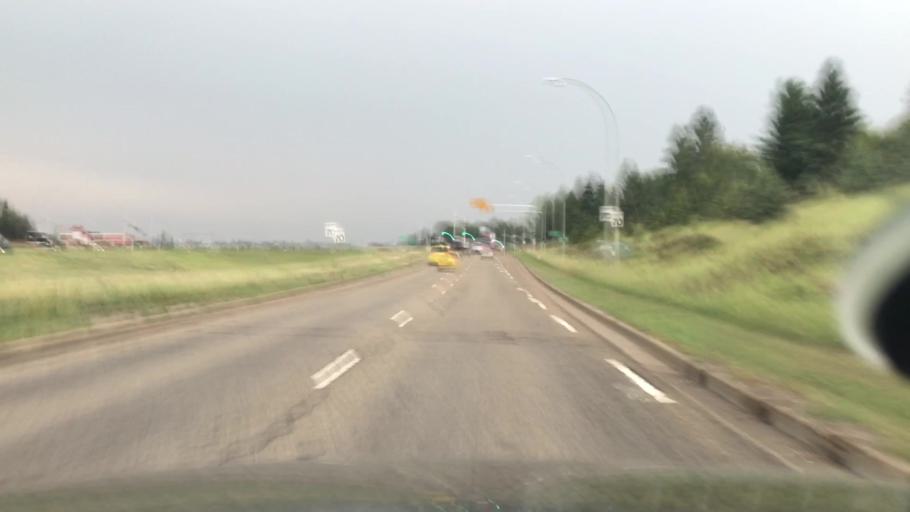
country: CA
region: Alberta
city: Edmonton
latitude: 53.4787
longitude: -113.5737
